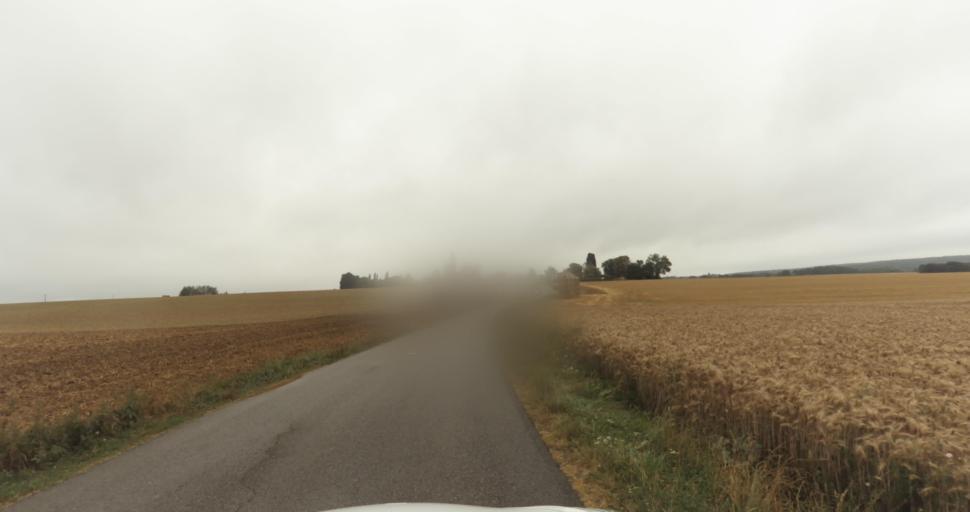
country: FR
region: Haute-Normandie
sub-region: Departement de l'Eure
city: Gravigny
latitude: 49.0784
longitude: 1.2143
